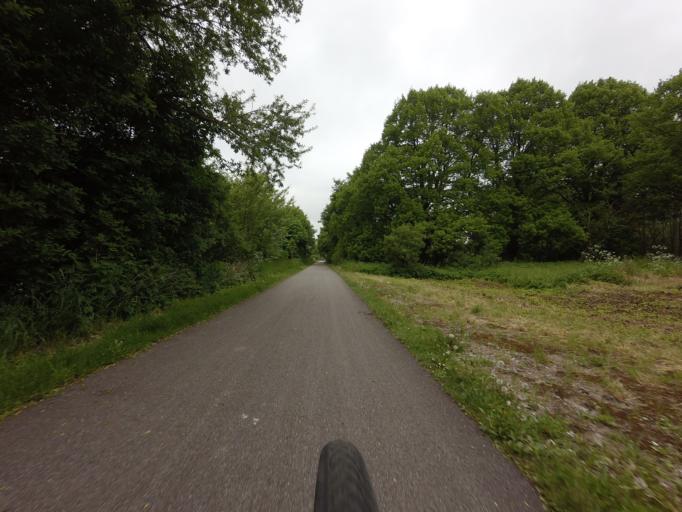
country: DK
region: Zealand
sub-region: Slagelse Kommune
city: Slagelse
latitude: 55.2959
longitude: 11.4180
